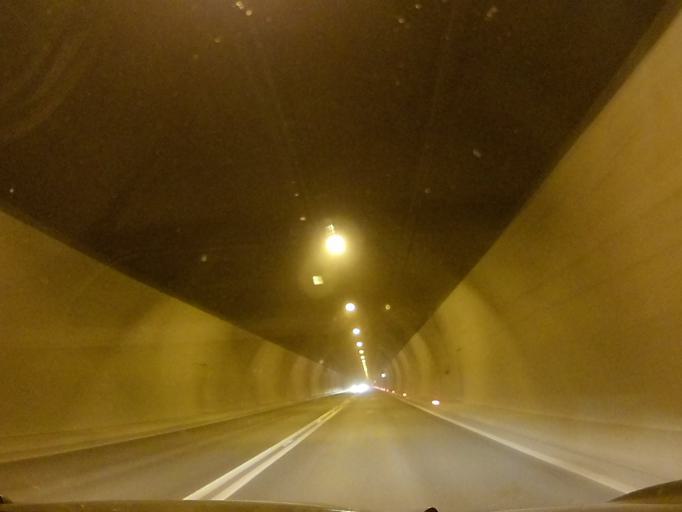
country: AT
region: Salzburg
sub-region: Politischer Bezirk Sankt Johann im Pongau
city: Schwarzach im Pongau
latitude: 47.3192
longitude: 13.1385
